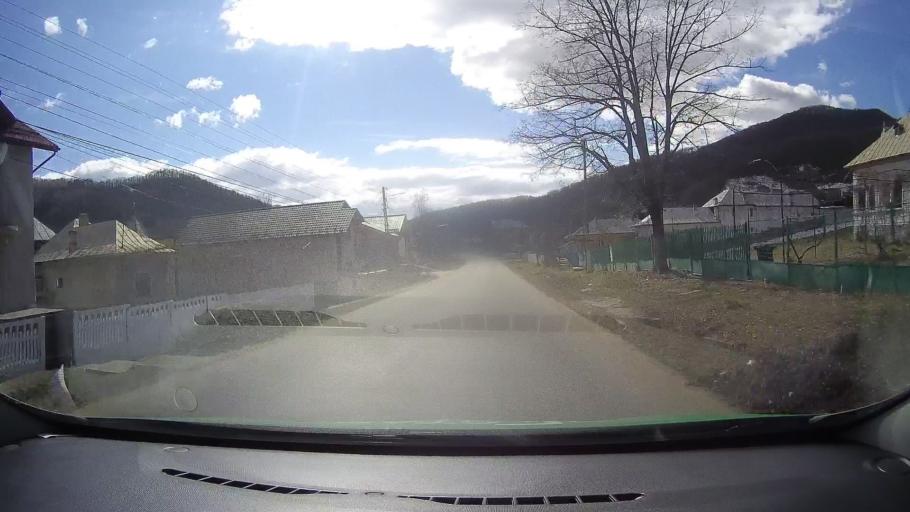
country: RO
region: Dambovita
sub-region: Comuna Vulcana Bai
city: Vulcana Bai
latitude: 45.0669
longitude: 25.3782
